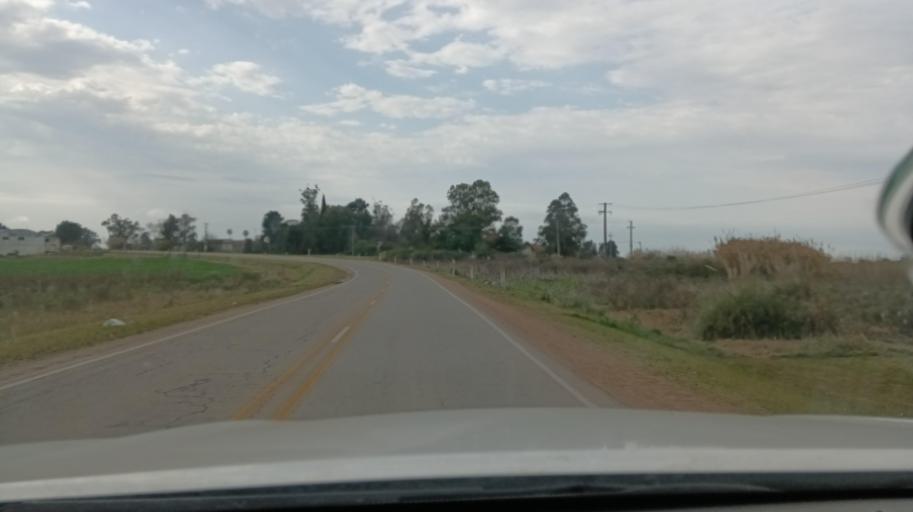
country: UY
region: Canelones
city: Toledo
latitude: -34.7076
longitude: -56.1063
